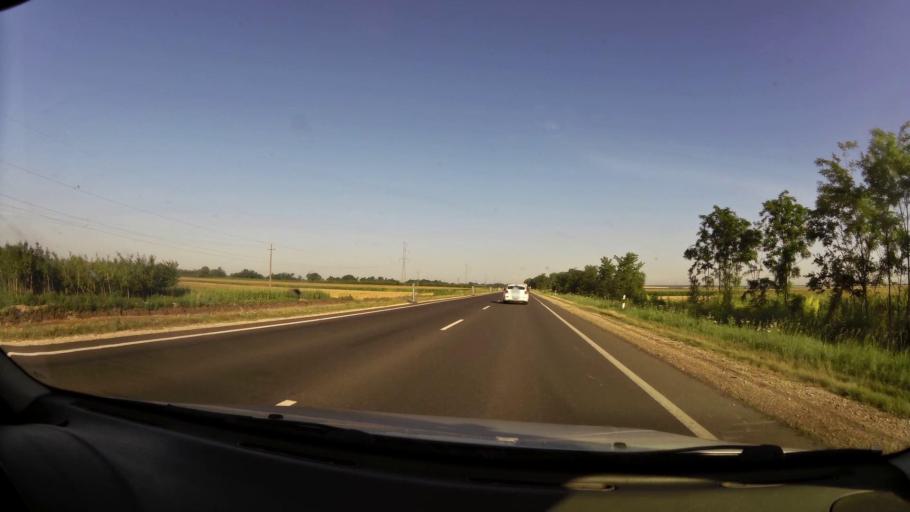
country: HU
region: Pest
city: Cegledbercel
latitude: 47.2159
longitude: 19.7235
